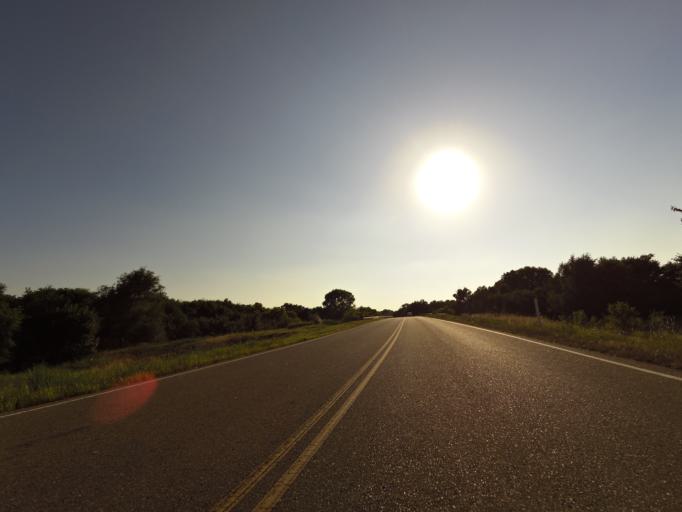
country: US
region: Kansas
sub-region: Reno County
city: Buhler
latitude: 38.1488
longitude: -97.8327
